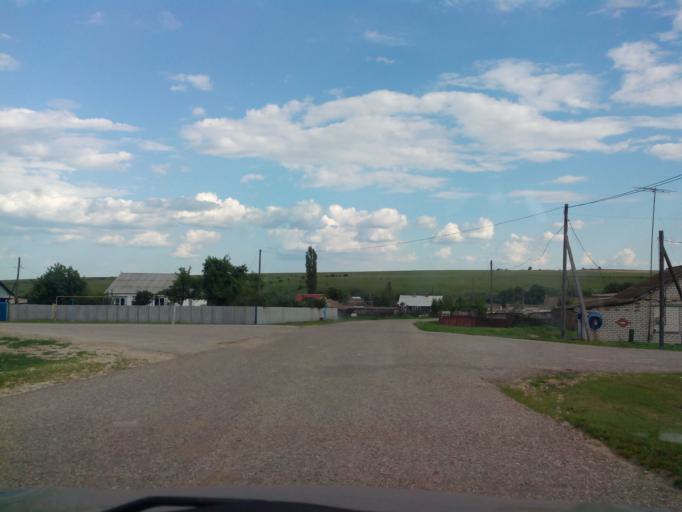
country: RU
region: Volgograd
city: Slashchevskaya
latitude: 49.7779
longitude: 42.4410
